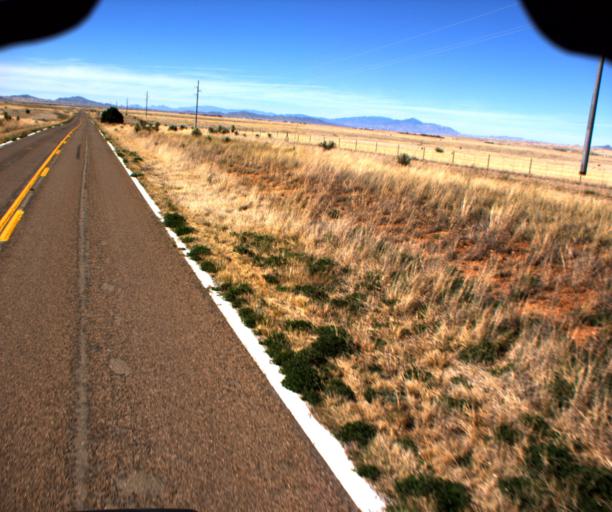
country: US
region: Arizona
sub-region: Cochise County
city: Huachuca City
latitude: 31.6297
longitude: -110.5946
